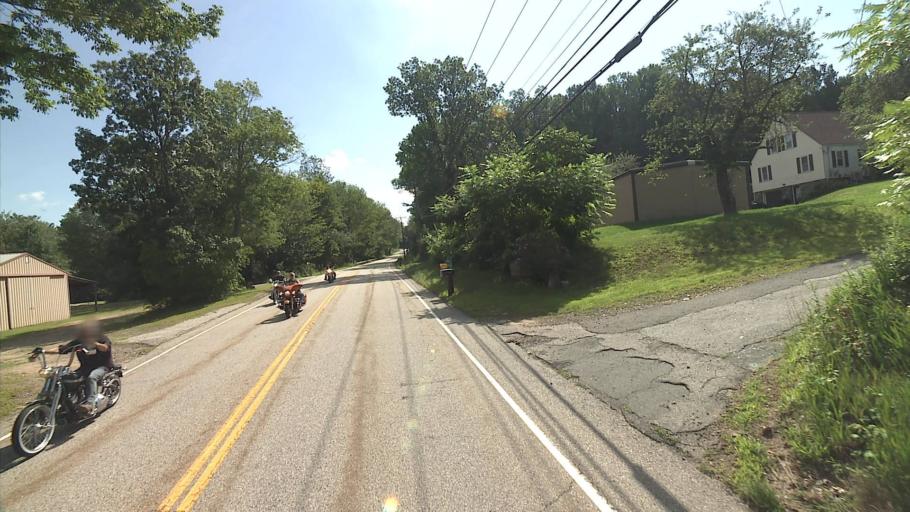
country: US
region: Connecticut
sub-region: Tolland County
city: Stafford
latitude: 41.9645
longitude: -72.2094
